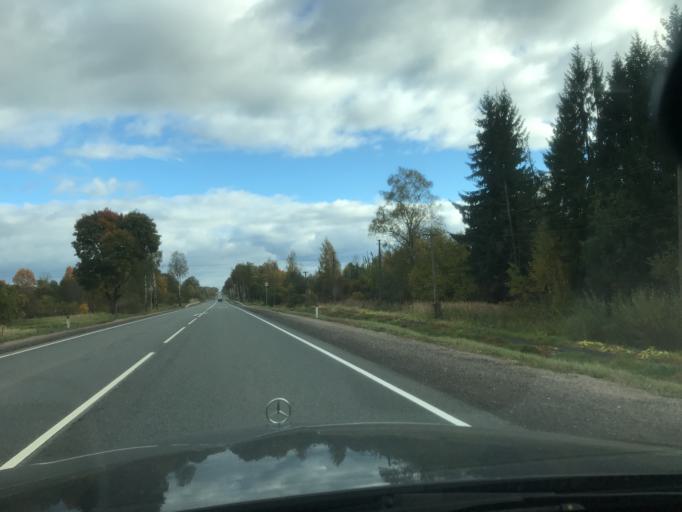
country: RU
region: Pskov
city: Opochka
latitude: 56.6714
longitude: 28.7271
